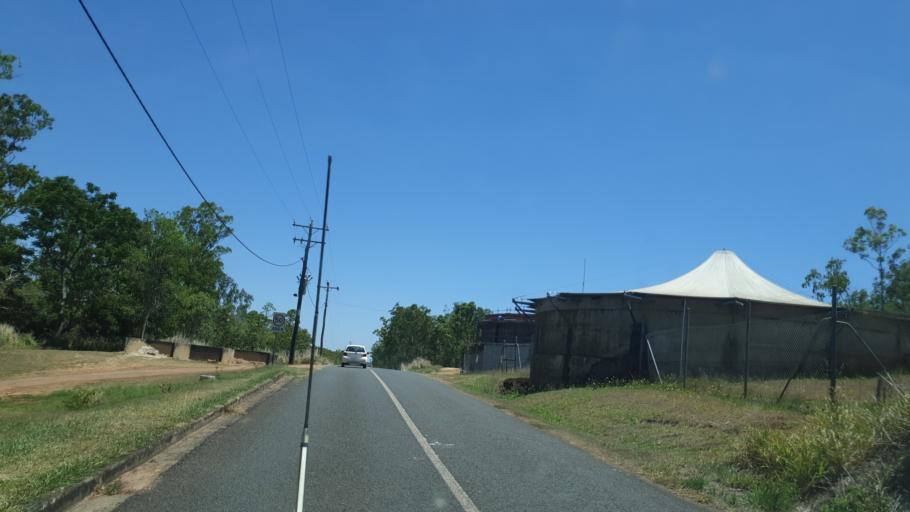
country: AU
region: Queensland
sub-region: Tablelands
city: Atherton
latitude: -17.2668
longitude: 145.4904
